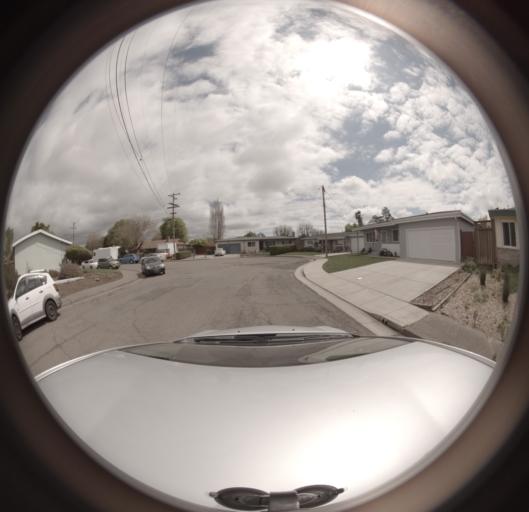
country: US
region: California
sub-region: Sonoma County
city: Petaluma
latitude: 38.2510
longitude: -122.6275
